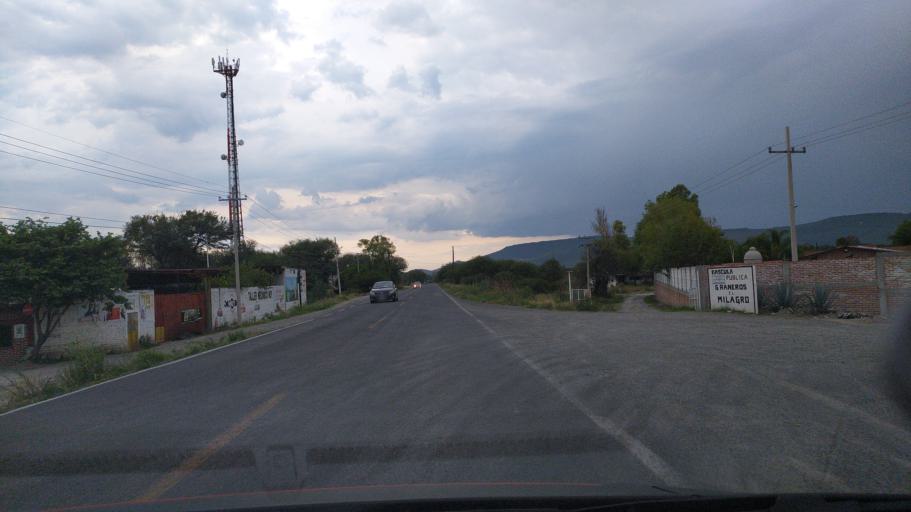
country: MX
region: Guanajuato
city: San Roque
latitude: 20.9719
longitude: -101.8581
